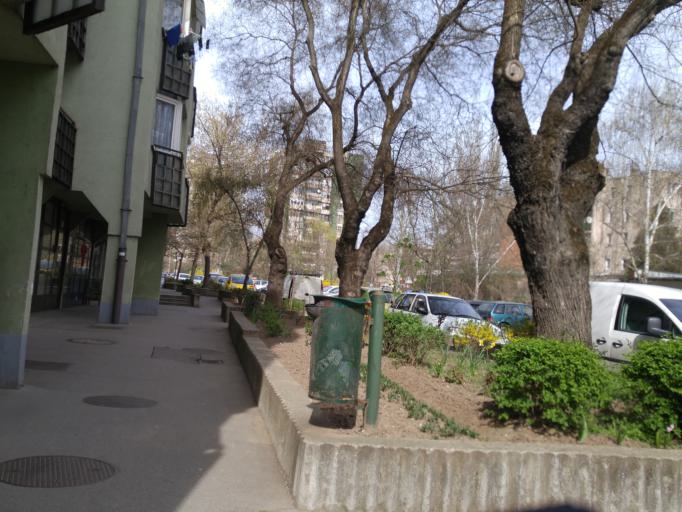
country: HU
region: Pest
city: Vac
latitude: 47.7711
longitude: 19.1391
